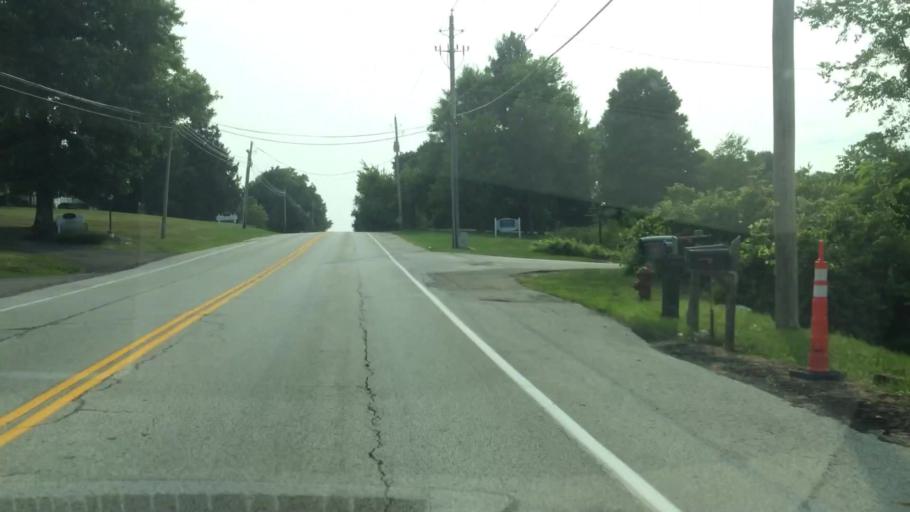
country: US
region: Ohio
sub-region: Summit County
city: Tallmadge
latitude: 41.0955
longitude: -81.4506
